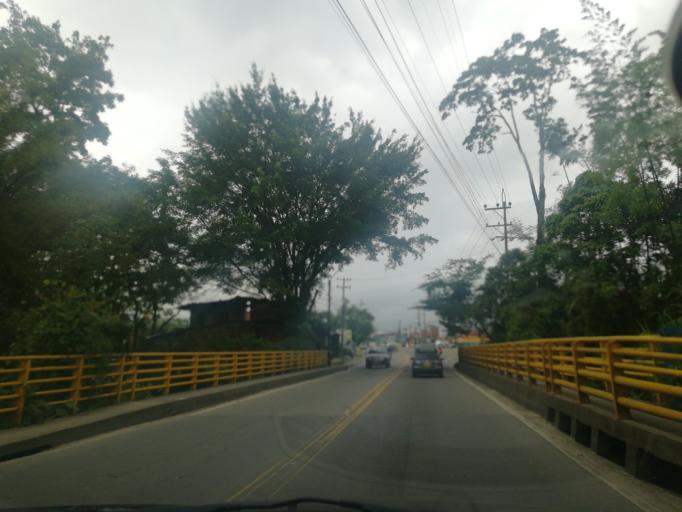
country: CO
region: Meta
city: Acacias
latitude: 3.9906
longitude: -73.7656
